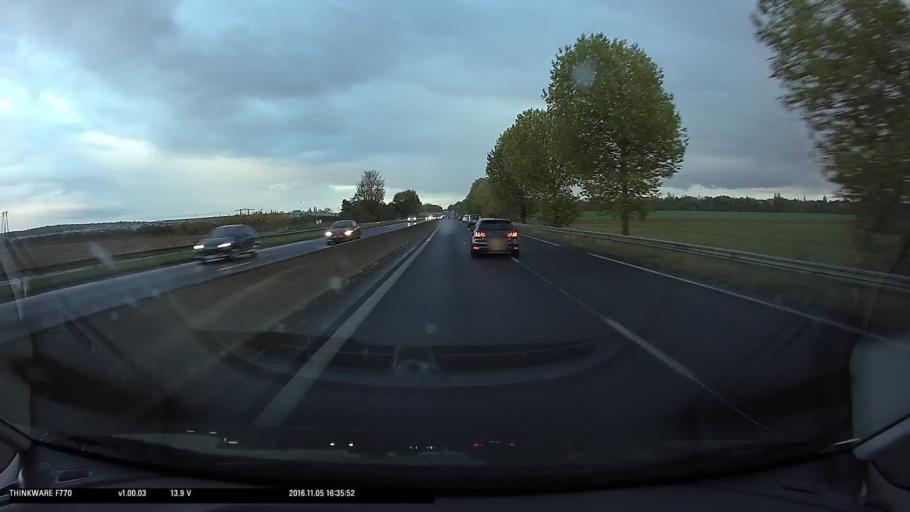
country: FR
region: Ile-de-France
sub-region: Departement du Val-d'Oise
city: Courdimanche
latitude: 49.0619
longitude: 1.9905
